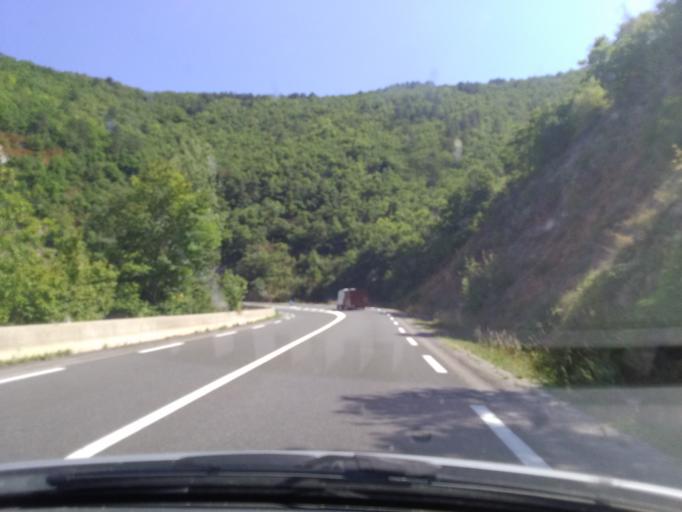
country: FR
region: Midi-Pyrenees
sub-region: Departement de l'Aveyron
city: Millau
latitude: 44.0917
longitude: 3.1135
